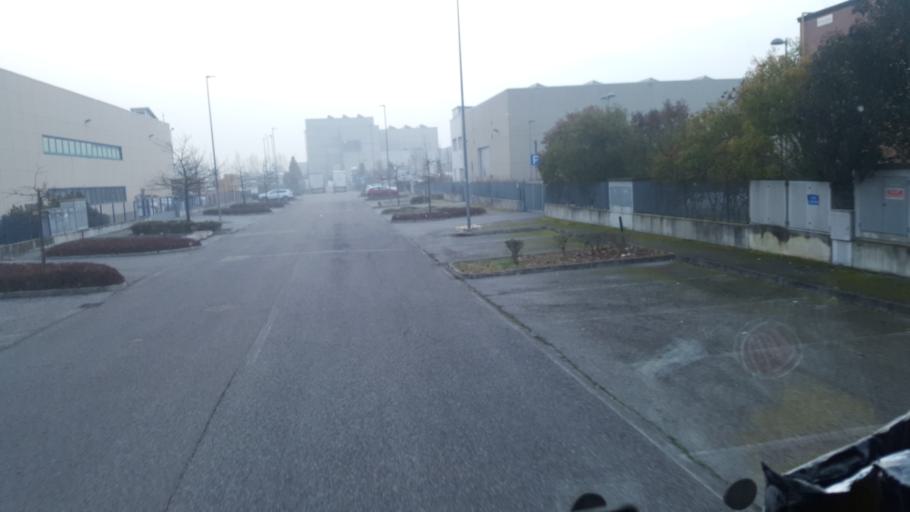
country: IT
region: Emilia-Romagna
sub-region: Provincia di Ravenna
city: Faenza
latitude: 44.3044
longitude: 11.8974
